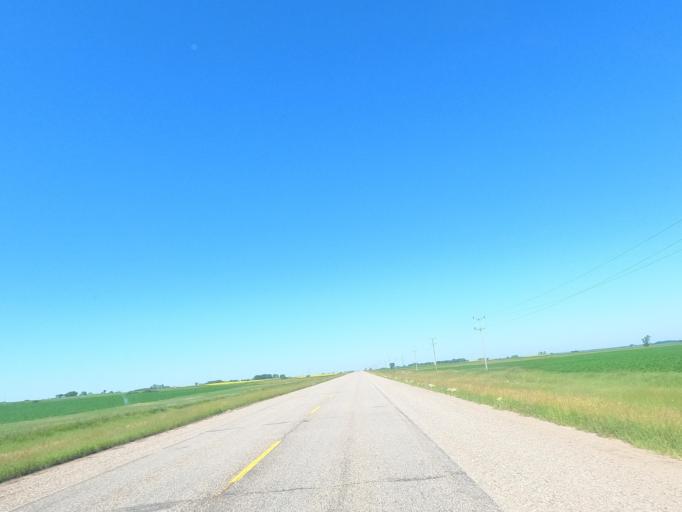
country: CA
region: Manitoba
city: Carberry
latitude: 49.5620
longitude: -99.5476
